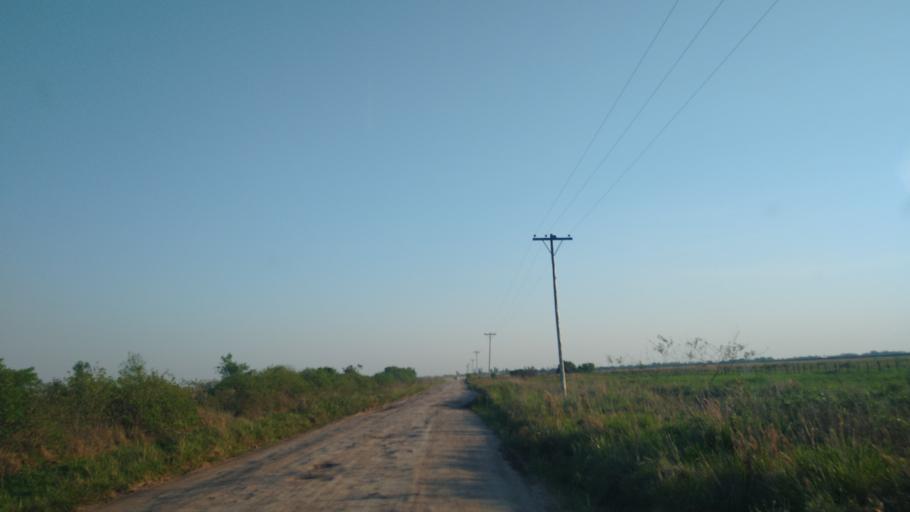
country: PY
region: Neembucu
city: Cerrito
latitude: -27.3927
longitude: -57.6588
